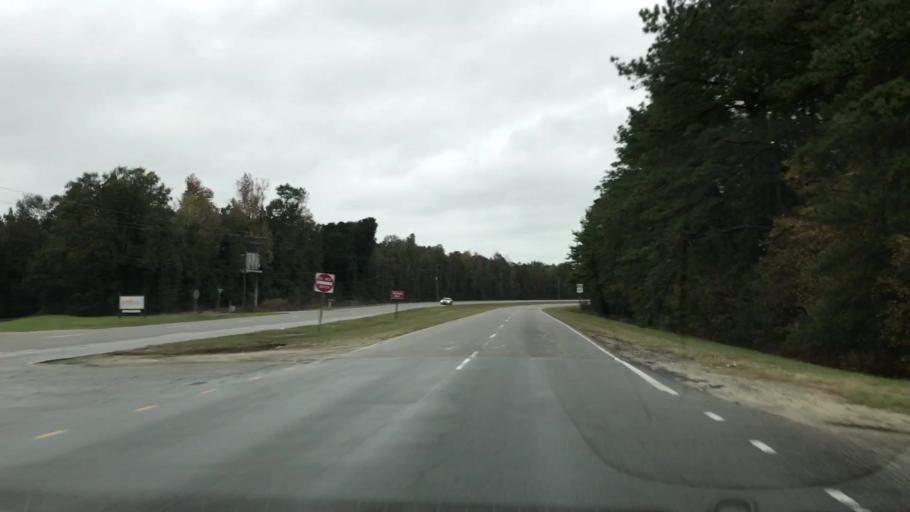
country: US
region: South Carolina
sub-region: Georgetown County
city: Georgetown
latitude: 33.2926
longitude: -79.3469
